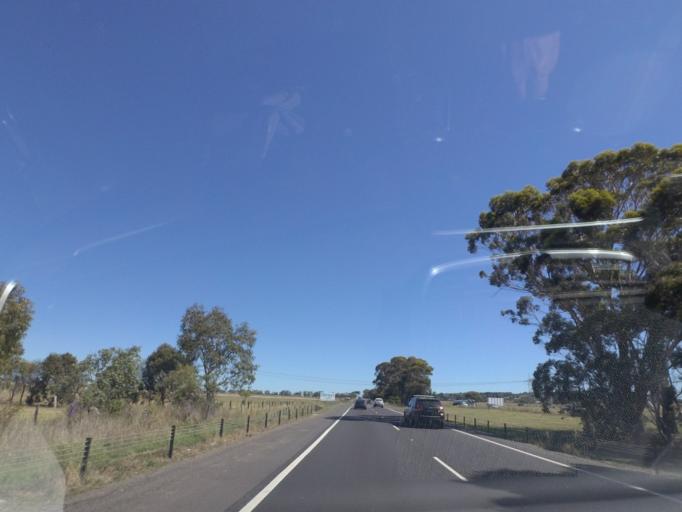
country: AU
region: Victoria
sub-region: Hume
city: Craigieburn
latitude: -37.5508
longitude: 144.9440
